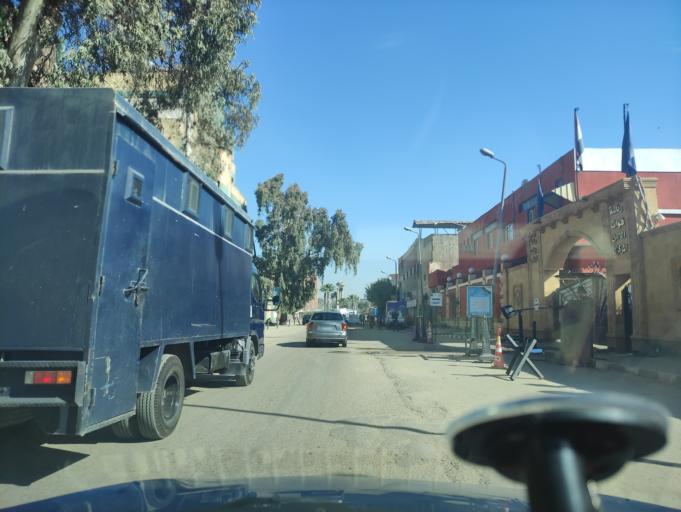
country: EG
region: Muhafazat al Qahirah
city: Cairo
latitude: 30.0545
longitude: 31.2761
